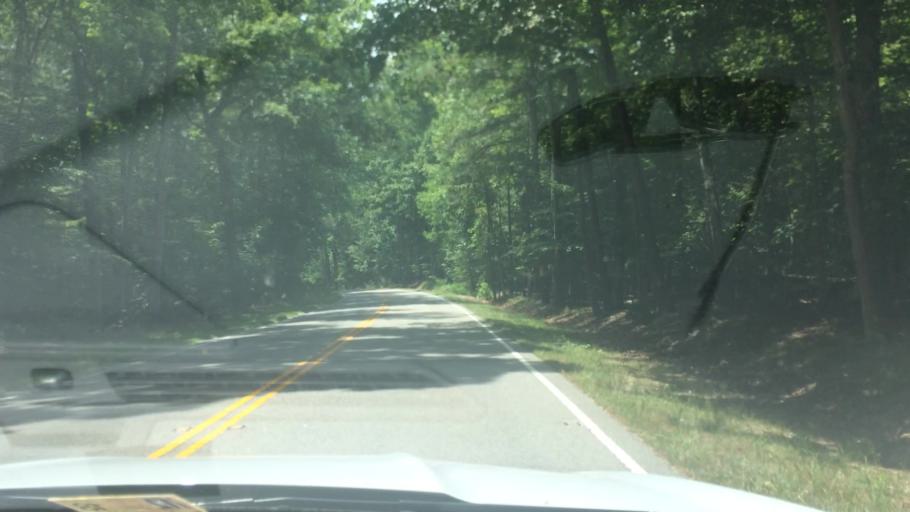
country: US
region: Virginia
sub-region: City of Williamsburg
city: Williamsburg
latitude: 37.3176
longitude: -76.7021
